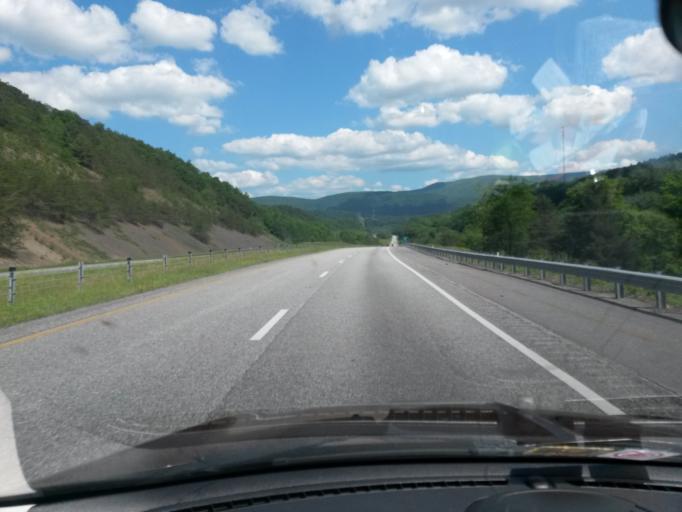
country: US
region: Virginia
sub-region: City of Covington
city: Covington
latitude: 37.7847
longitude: -80.0136
